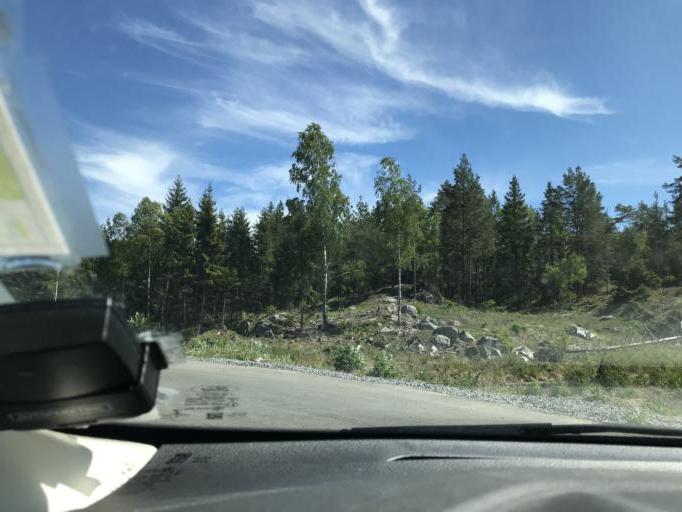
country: SE
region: Stockholm
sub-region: Botkyrka Kommun
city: Alby
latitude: 59.2137
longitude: 17.8492
